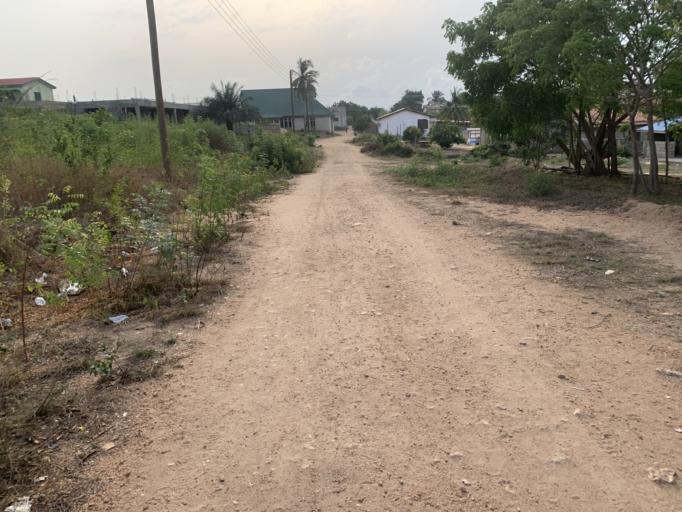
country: GH
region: Central
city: Winneba
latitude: 5.3606
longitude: -0.6257
